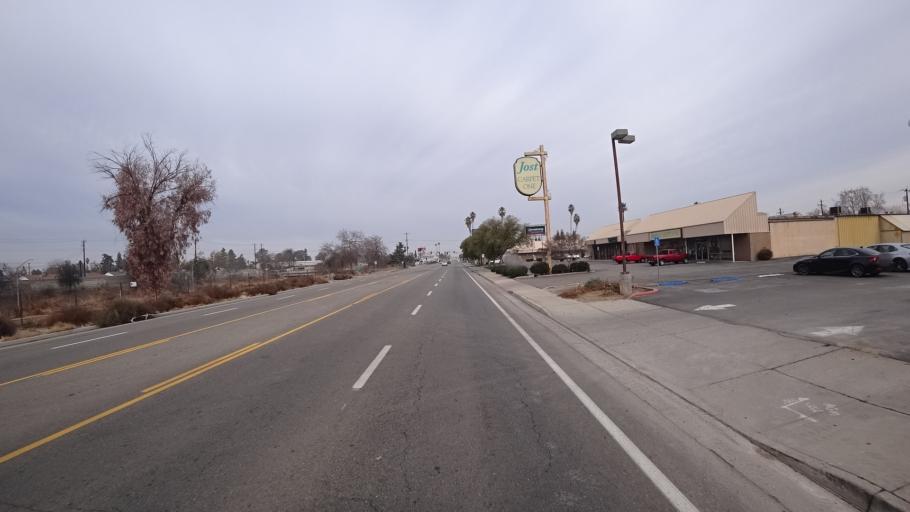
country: US
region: California
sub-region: Kern County
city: Bakersfield
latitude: 35.3595
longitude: -119.0388
